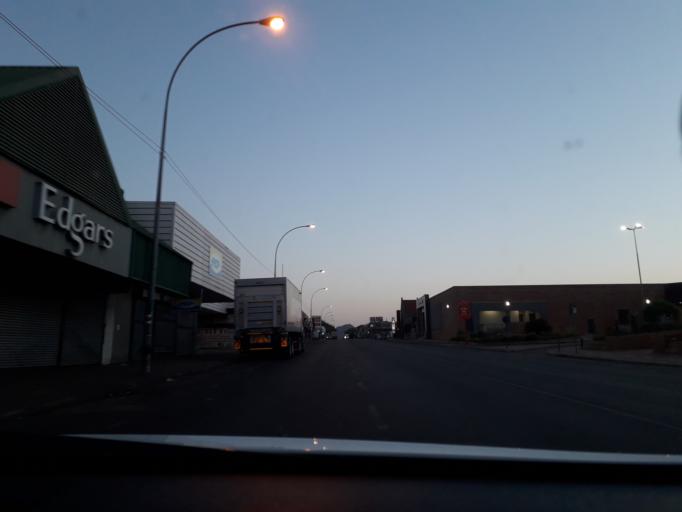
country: ZA
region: Limpopo
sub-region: Waterberg District Municipality
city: Mokopane
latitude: -24.1828
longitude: 29.0132
